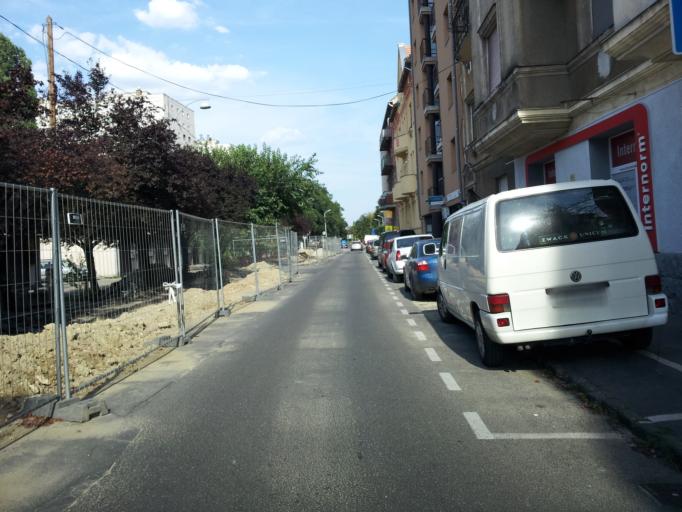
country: HU
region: Budapest
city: Budapest III. keruelet
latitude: 47.5388
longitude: 19.0344
